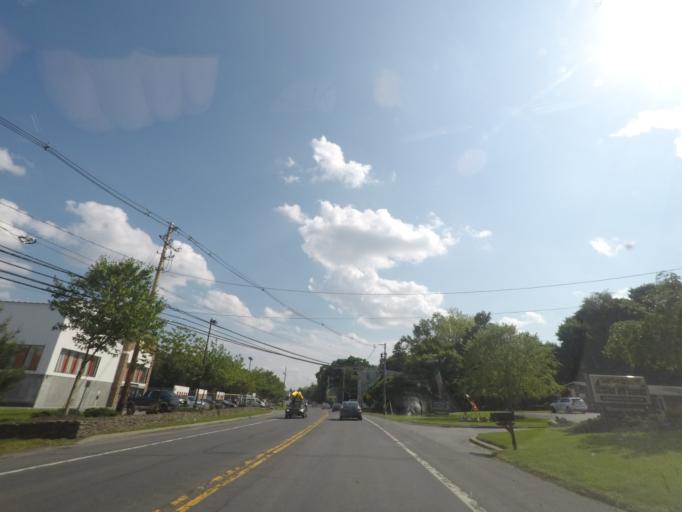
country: US
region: New York
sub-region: Orange County
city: Balmville
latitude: 41.5609
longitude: -74.0030
